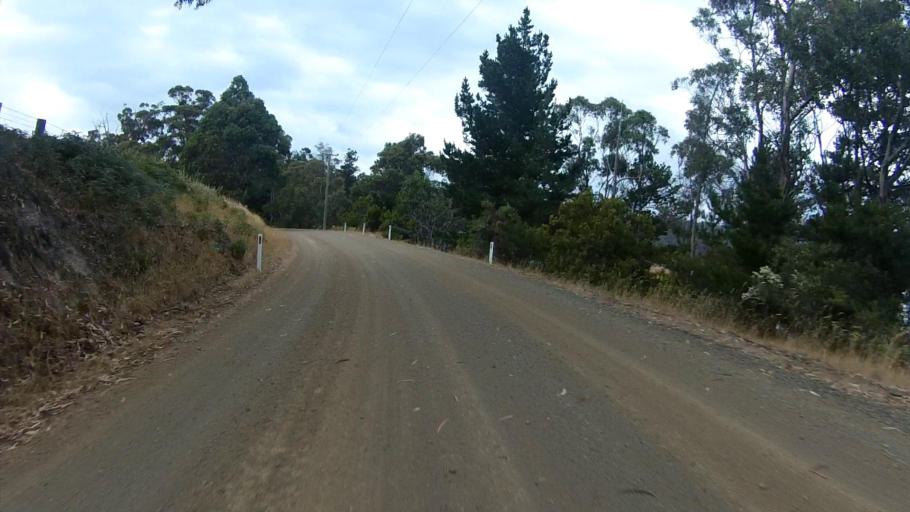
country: AU
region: Tasmania
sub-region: Huon Valley
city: Cygnet
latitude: -43.2360
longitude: 147.0988
